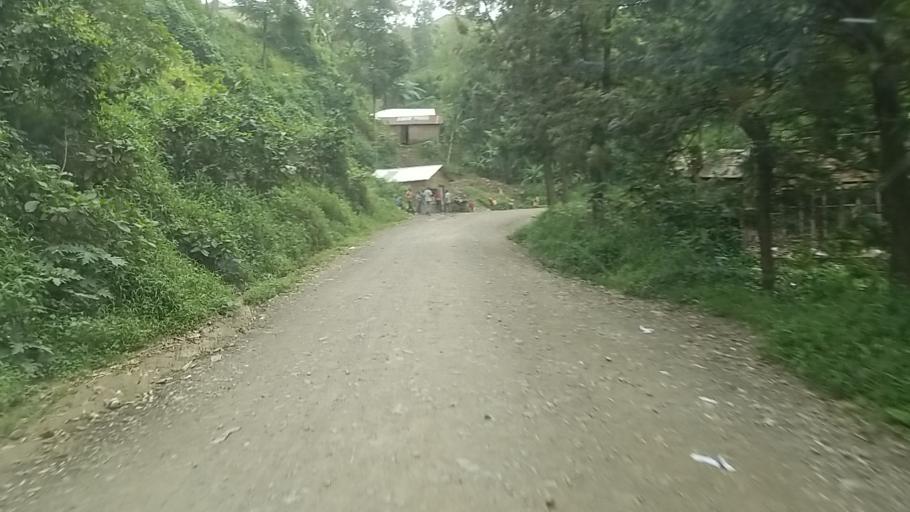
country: CD
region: Nord Kivu
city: Sake
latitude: -1.9221
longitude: 28.9407
